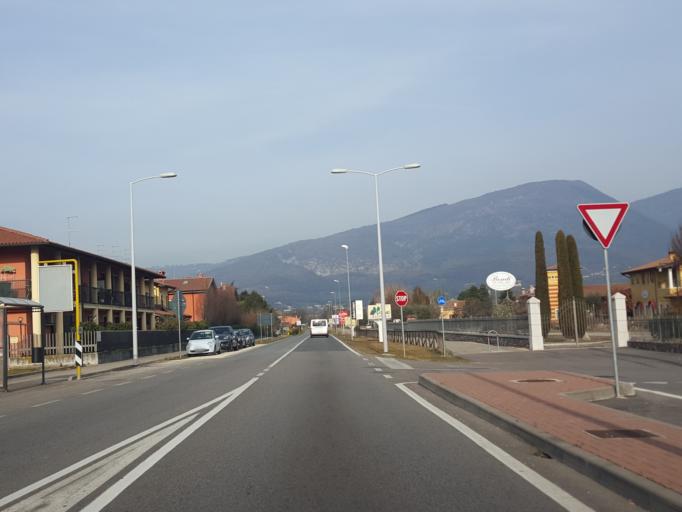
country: IT
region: Veneto
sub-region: Provincia di Verona
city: Costermano
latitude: 45.5732
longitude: 10.7580
